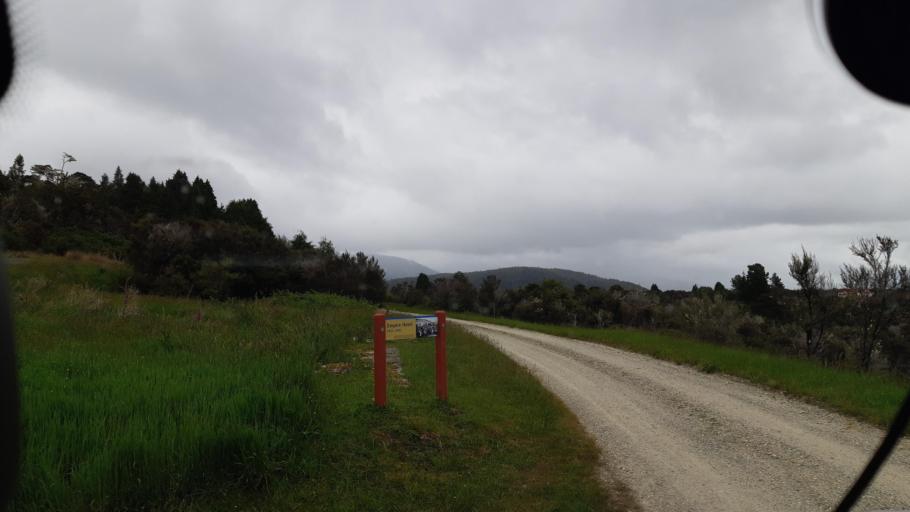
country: NZ
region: West Coast
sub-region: Buller District
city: Westport
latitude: -42.2896
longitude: 171.8194
